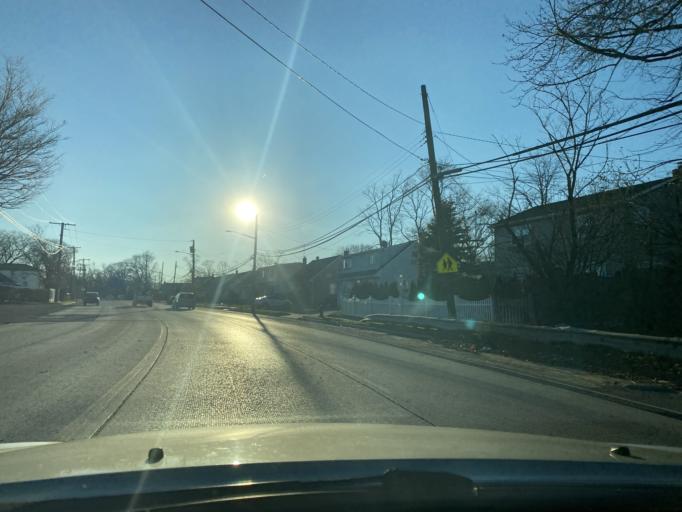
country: US
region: New York
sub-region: Nassau County
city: Inwood
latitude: 40.6219
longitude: -73.7481
